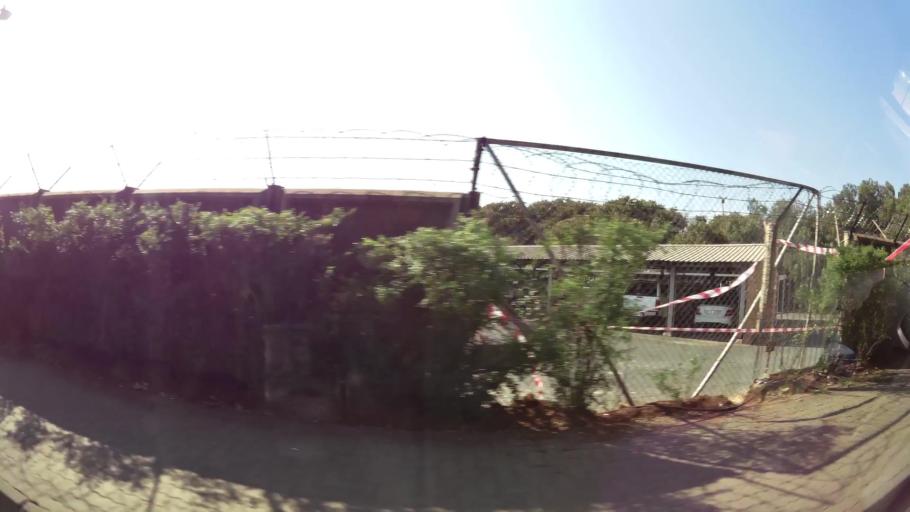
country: ZA
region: Gauteng
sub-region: Ekurhuleni Metropolitan Municipality
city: Boksburg
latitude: -26.1450
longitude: 28.2241
